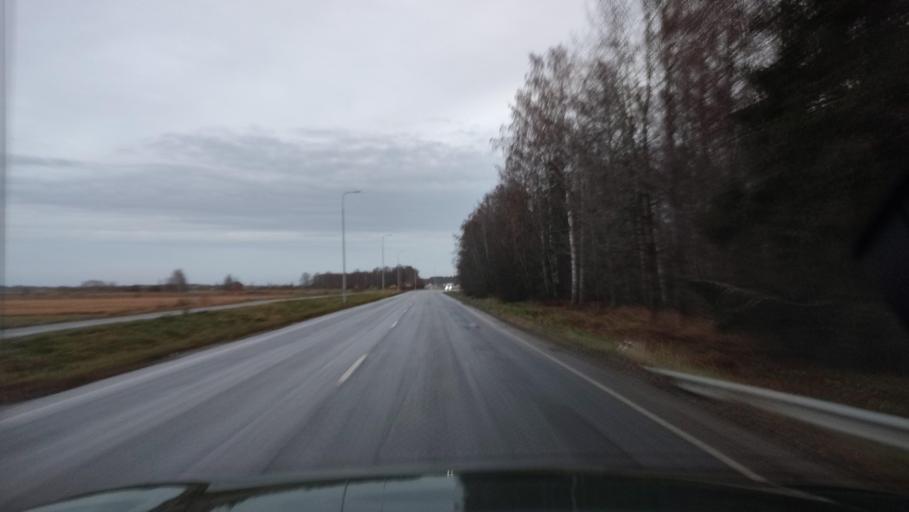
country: FI
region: Ostrobothnia
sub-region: Vaasa
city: Ristinummi
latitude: 63.0449
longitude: 21.7346
